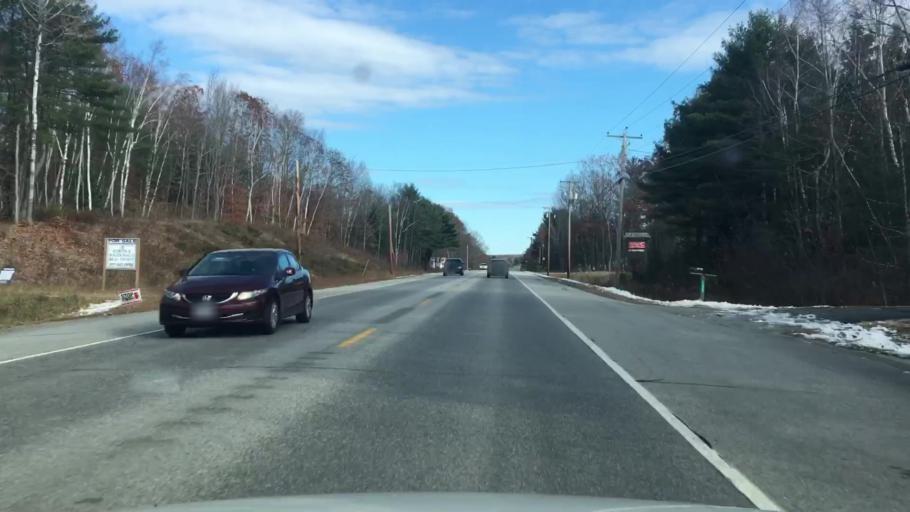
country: US
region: Maine
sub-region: Kennebec County
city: Winthrop
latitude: 44.3128
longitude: -69.9458
